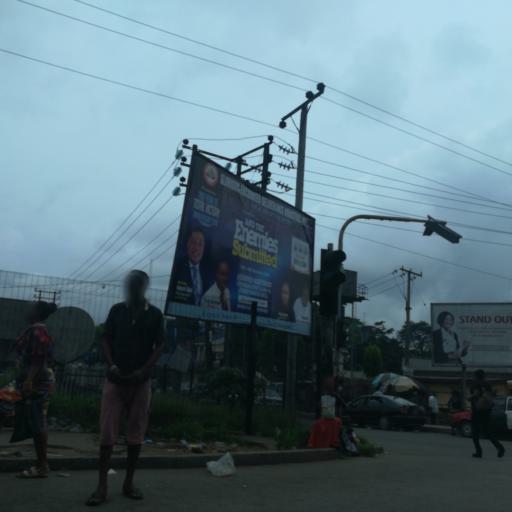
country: NG
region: Rivers
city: Port Harcourt
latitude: 4.7890
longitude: 7.0031
